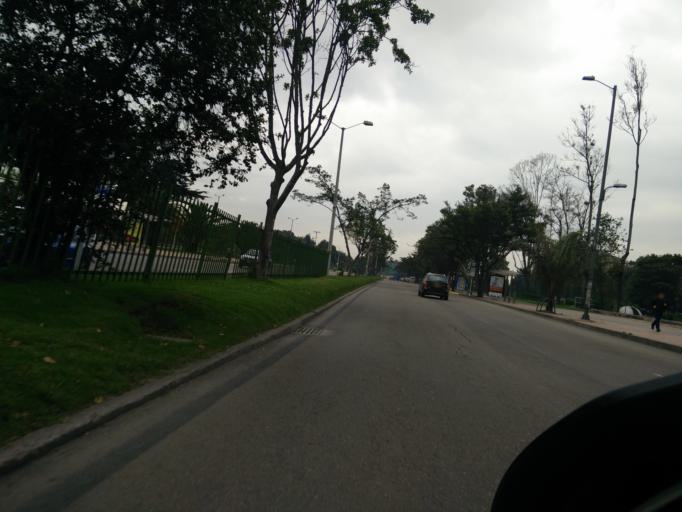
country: CO
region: Bogota D.C.
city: Bogota
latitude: 4.6605
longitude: -74.0893
